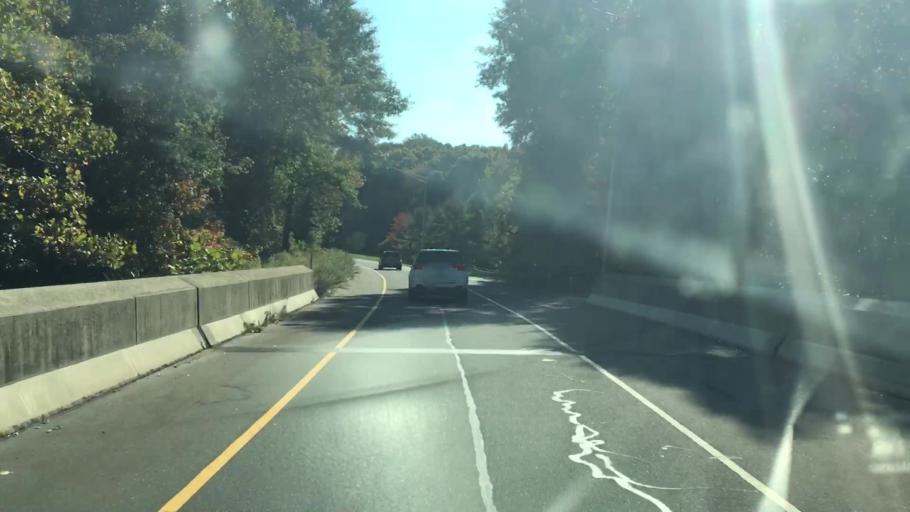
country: US
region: Connecticut
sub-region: Fairfield County
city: Trumbull
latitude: 41.2353
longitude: -73.1921
